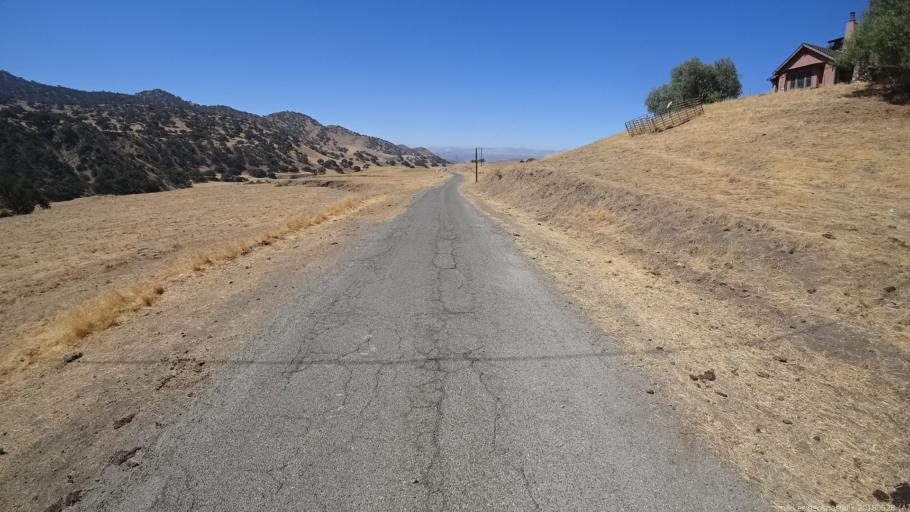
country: US
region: California
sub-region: San Luis Obispo County
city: San Miguel
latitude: 36.0657
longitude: -120.7844
